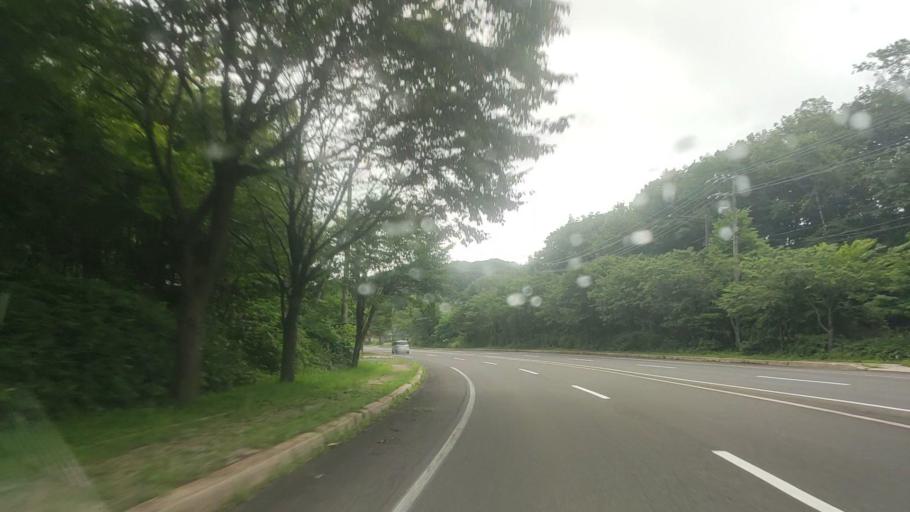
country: JP
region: Hokkaido
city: Shiraoi
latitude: 42.4701
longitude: 141.1498
